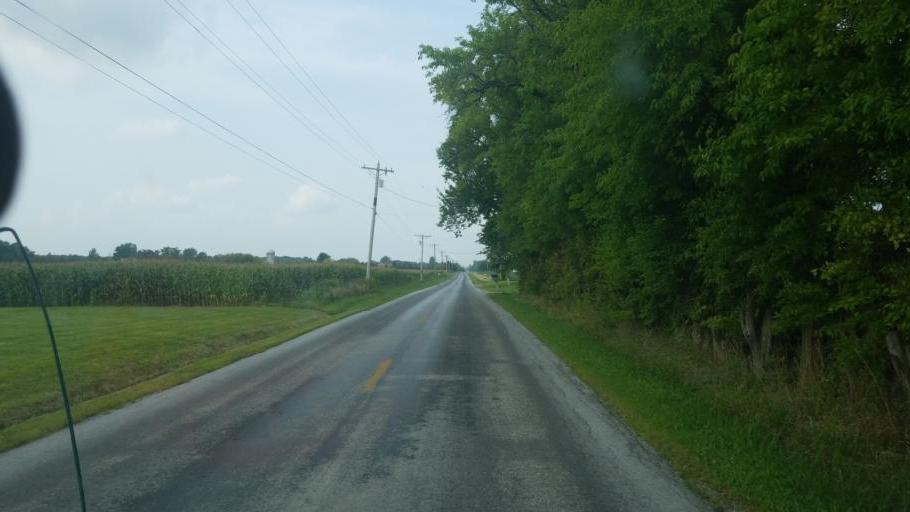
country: US
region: Ohio
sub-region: Lorain County
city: Wellington
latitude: 41.0818
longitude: -82.1618
